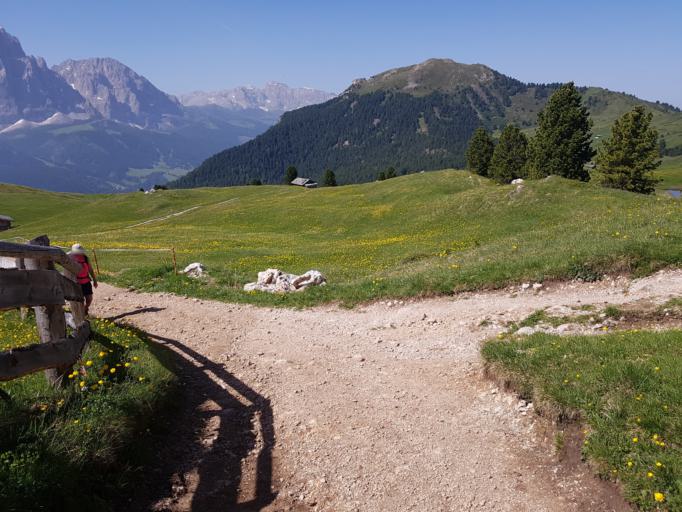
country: IT
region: Trentino-Alto Adige
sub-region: Bolzano
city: Santa Cristina Valgardena
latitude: 46.5933
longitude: 11.7446
